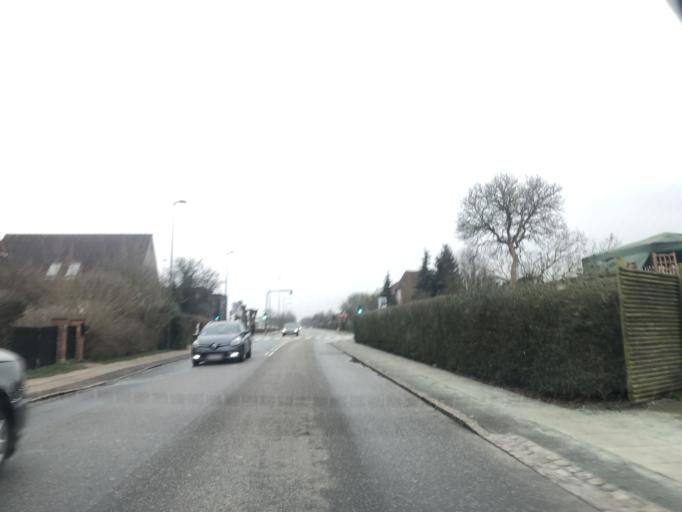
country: DK
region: Capital Region
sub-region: Tarnby Kommune
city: Tarnby
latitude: 55.6435
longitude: 12.6065
